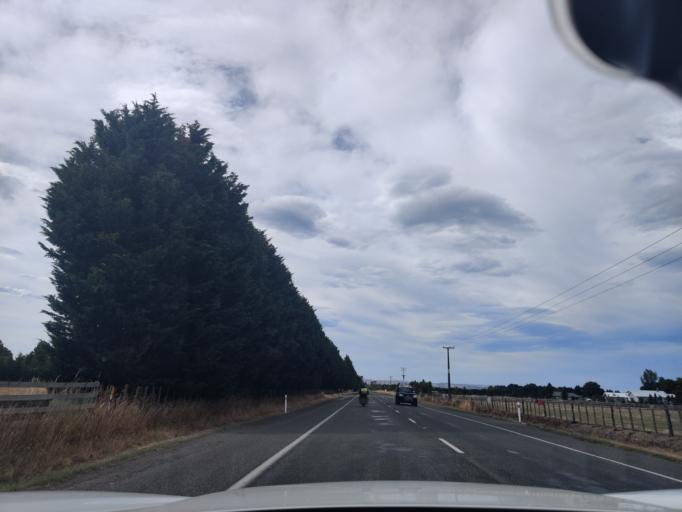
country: NZ
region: Wellington
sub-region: Masterton District
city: Masterton
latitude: -40.9018
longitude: 175.6640
